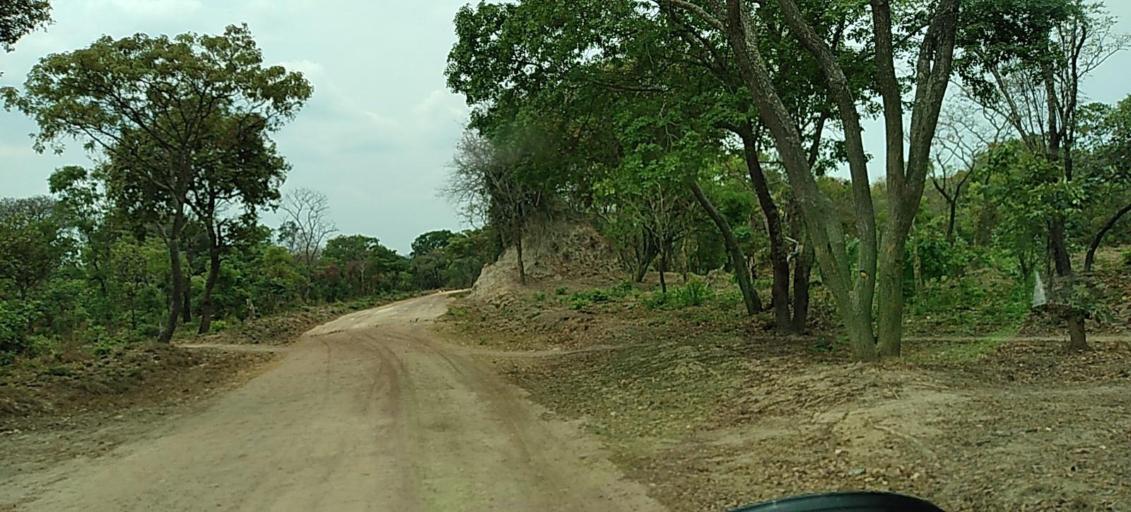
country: ZM
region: North-Western
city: Solwezi
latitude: -12.7839
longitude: 26.5176
